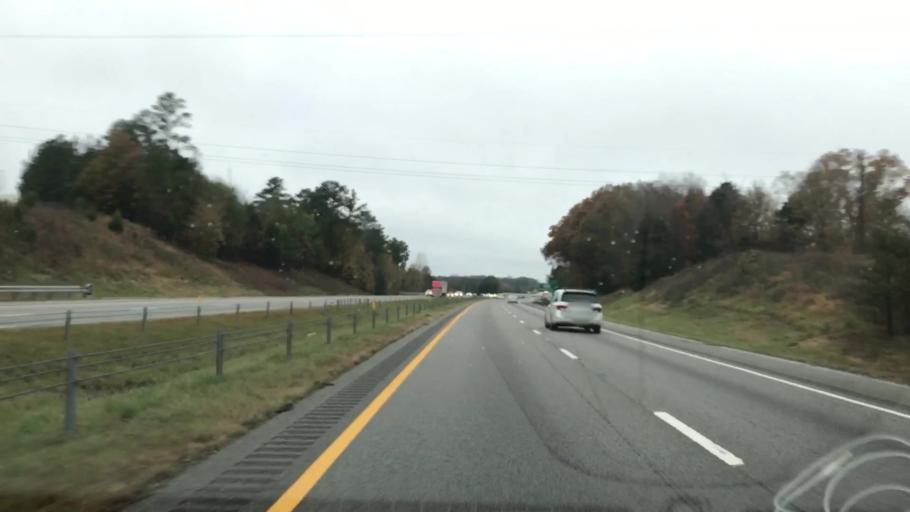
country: US
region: South Carolina
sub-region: Newberry County
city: Prosperity
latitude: 34.2887
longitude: -81.5388
